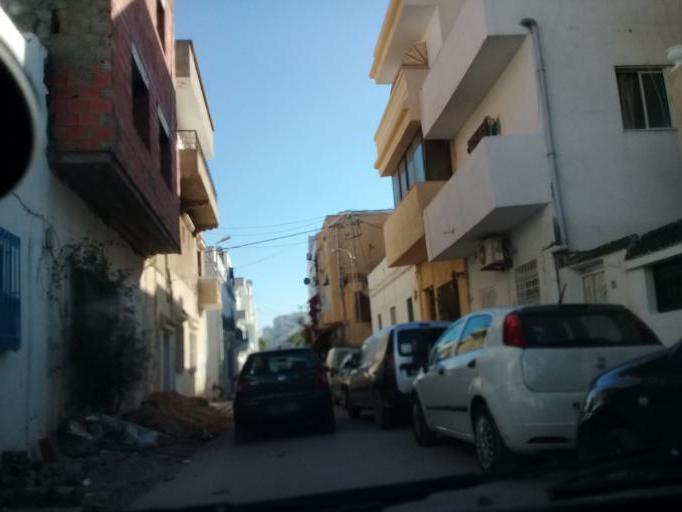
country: TN
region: Tunis
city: La Goulette
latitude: 36.8218
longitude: 10.3089
